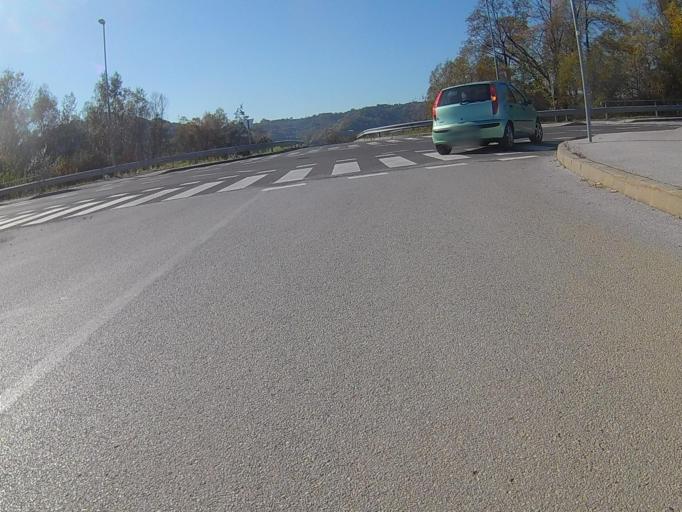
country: SI
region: Pesnica
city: Pesnica pri Mariboru
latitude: 46.5822
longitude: 15.7247
